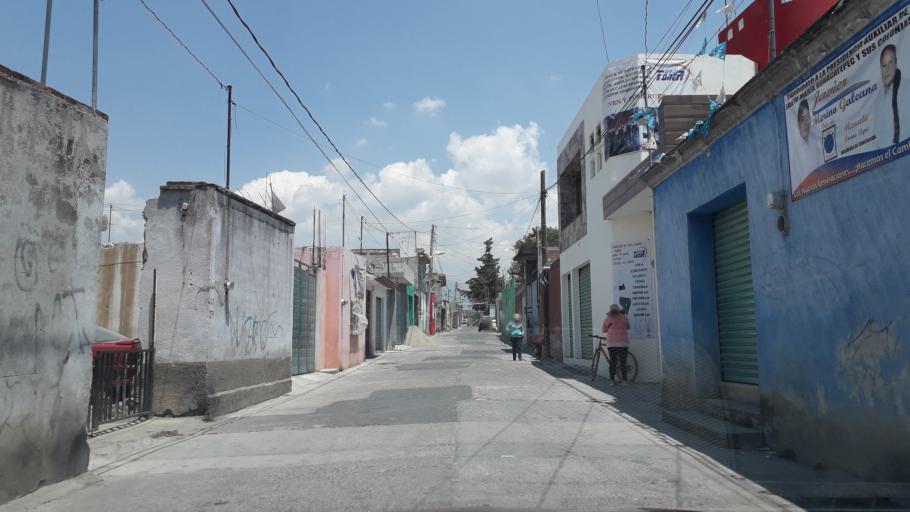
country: MX
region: Puebla
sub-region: Puebla
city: Santa Maria Xonacatepec
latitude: 19.0888
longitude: -98.1042
